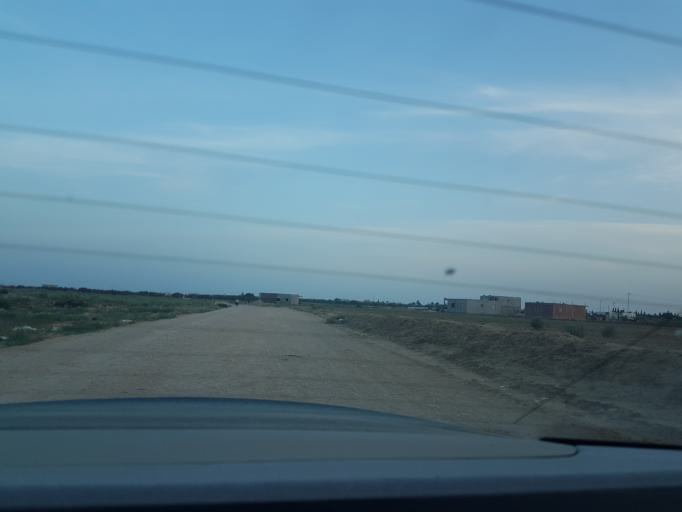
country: TN
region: Safaqis
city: Sfax
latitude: 34.7086
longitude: 10.6892
